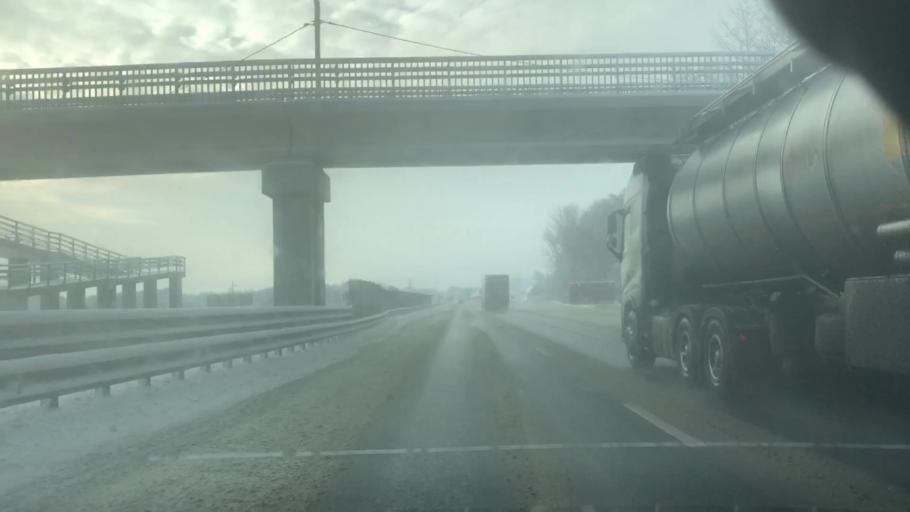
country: RU
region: Tula
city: Venev
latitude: 54.3954
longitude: 38.1572
